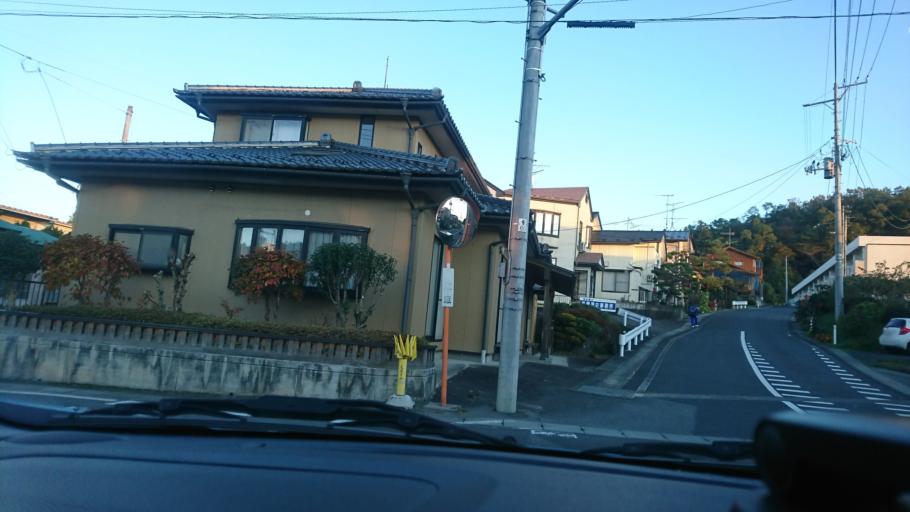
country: JP
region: Iwate
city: Ichinoseki
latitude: 38.8606
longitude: 141.3497
